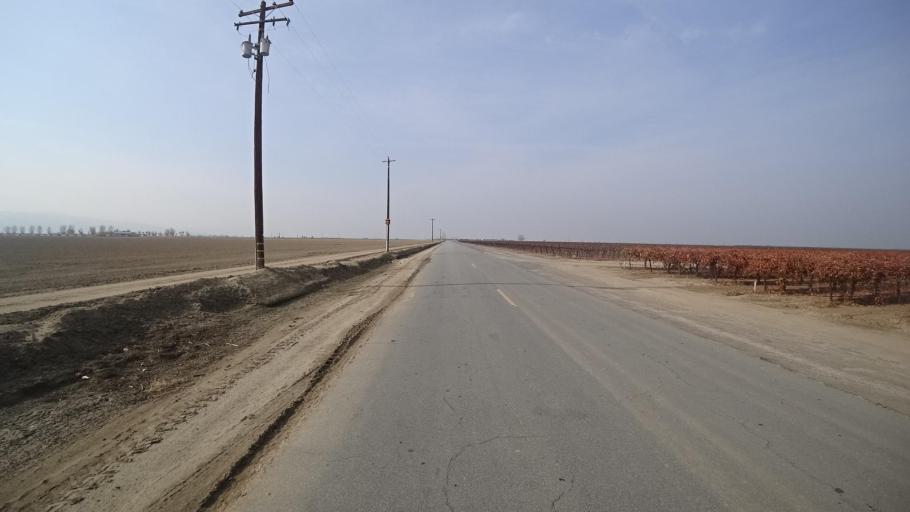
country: US
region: California
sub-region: Kern County
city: Weedpatch
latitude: 35.0754
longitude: -118.9492
